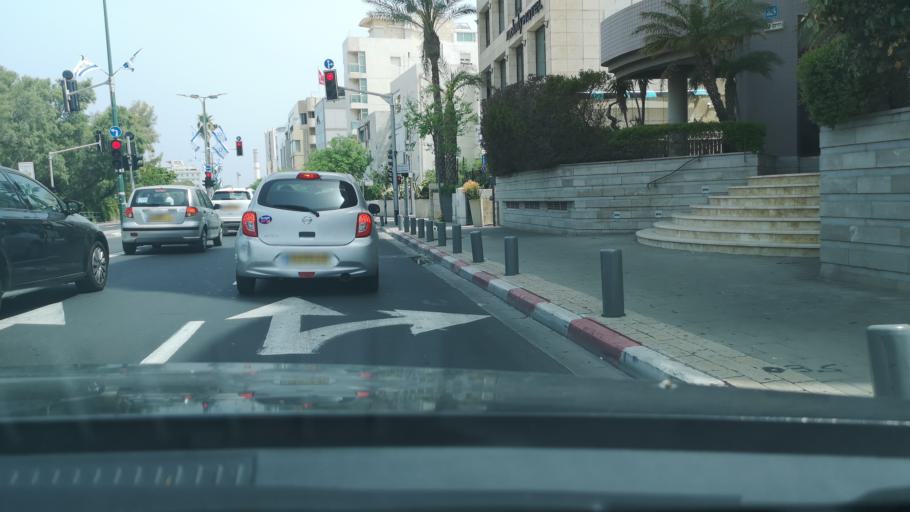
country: IL
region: Tel Aviv
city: Tel Aviv
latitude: 32.0895
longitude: 34.7721
